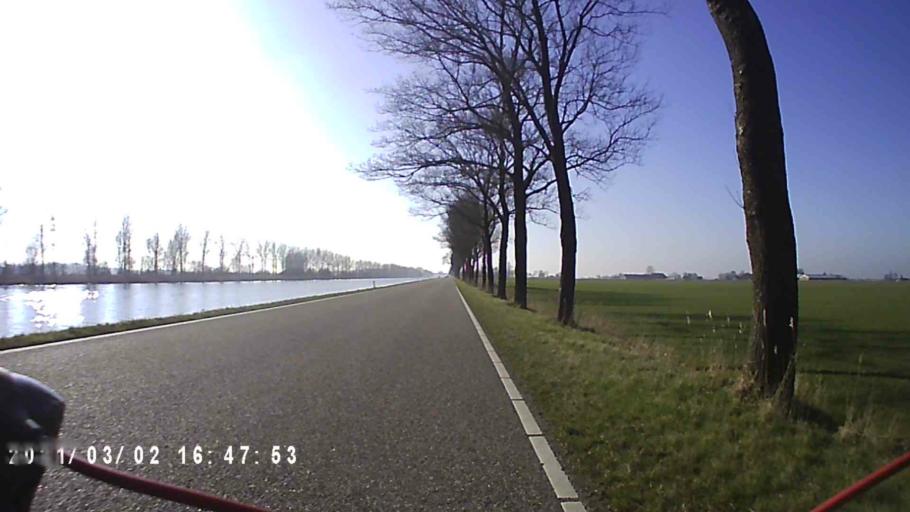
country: NL
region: Groningen
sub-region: Gemeente Grootegast
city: Grootegast
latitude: 53.2452
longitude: 6.2733
